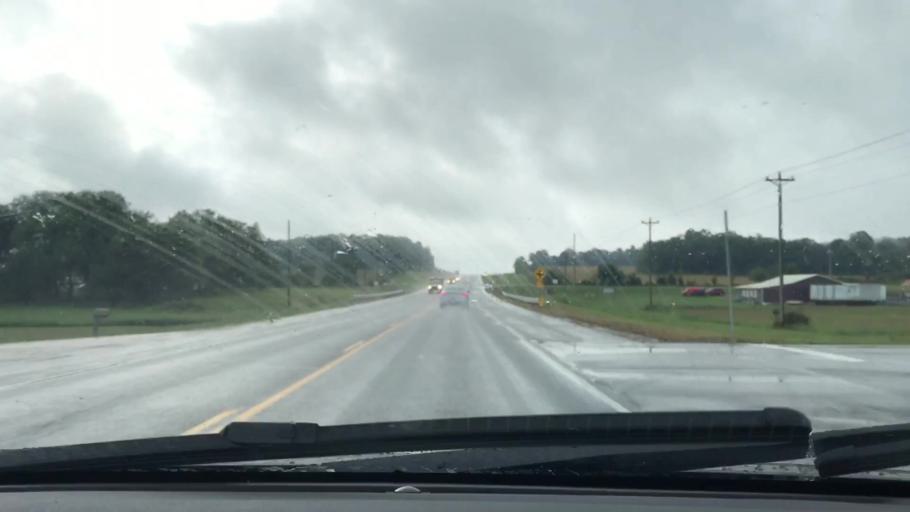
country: US
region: Tennessee
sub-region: Sumner County
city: Westmoreland
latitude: 36.5239
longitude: -86.1528
